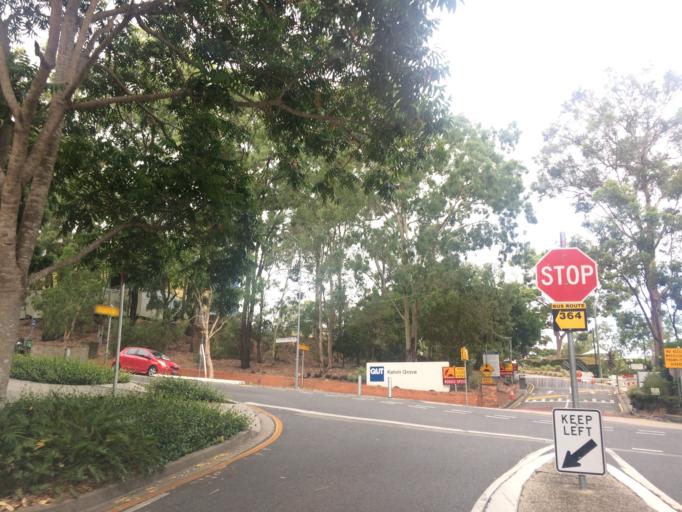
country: AU
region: Queensland
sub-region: Brisbane
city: Spring Hill
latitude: -27.4529
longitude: 153.0159
